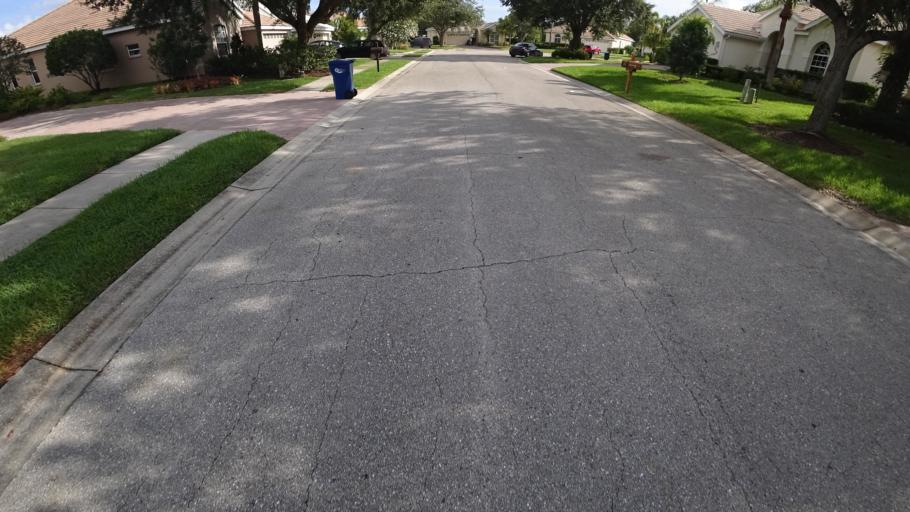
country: US
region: Florida
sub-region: Sarasota County
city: Desoto Lakes
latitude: 27.4166
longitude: -82.4773
